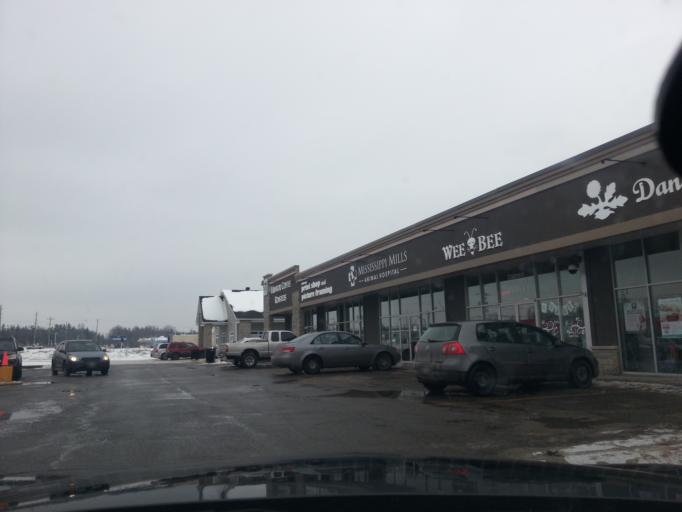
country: CA
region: Ontario
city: Carleton Place
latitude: 45.2350
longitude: -76.1817
